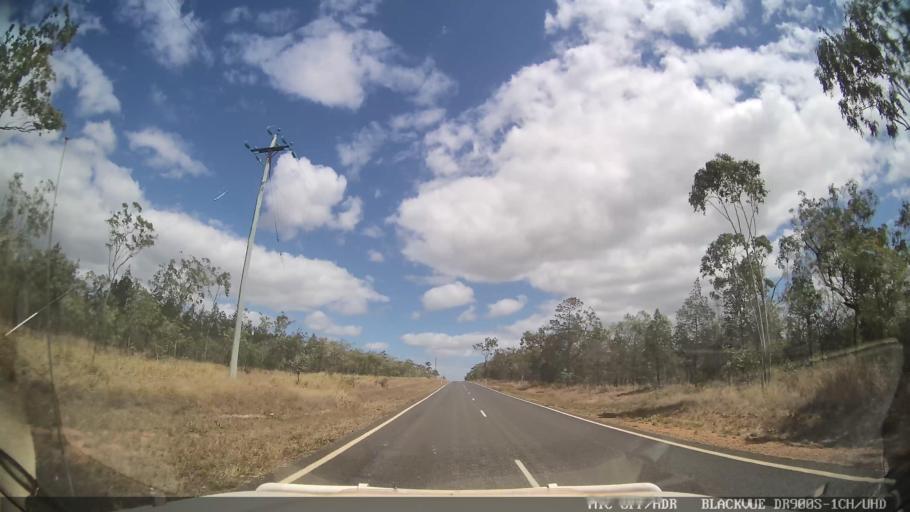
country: AU
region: Queensland
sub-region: Tablelands
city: Ravenshoe
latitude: -17.7286
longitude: 145.0461
